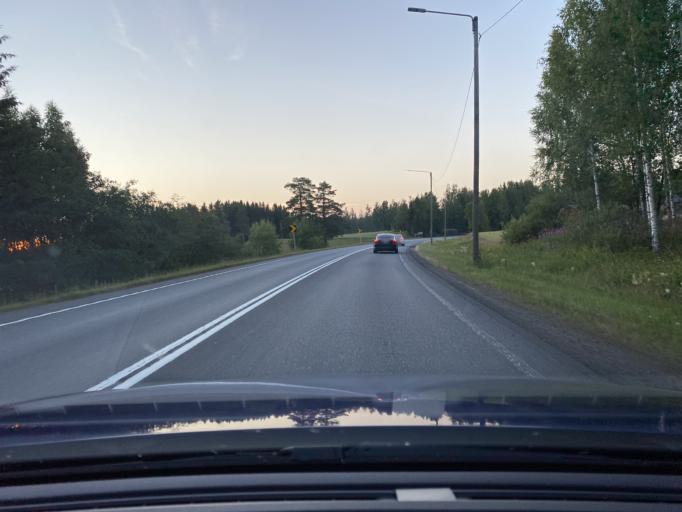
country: FI
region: Pirkanmaa
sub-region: Luoteis-Pirkanmaa
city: Ikaalinen
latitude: 61.8464
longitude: 22.9305
